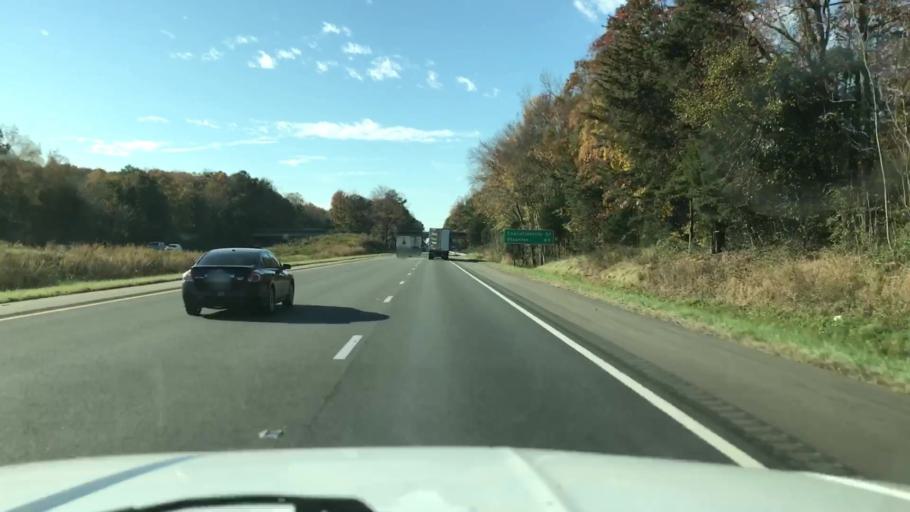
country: US
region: Virginia
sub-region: Henrico County
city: Wyndham
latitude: 37.6879
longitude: -77.6810
